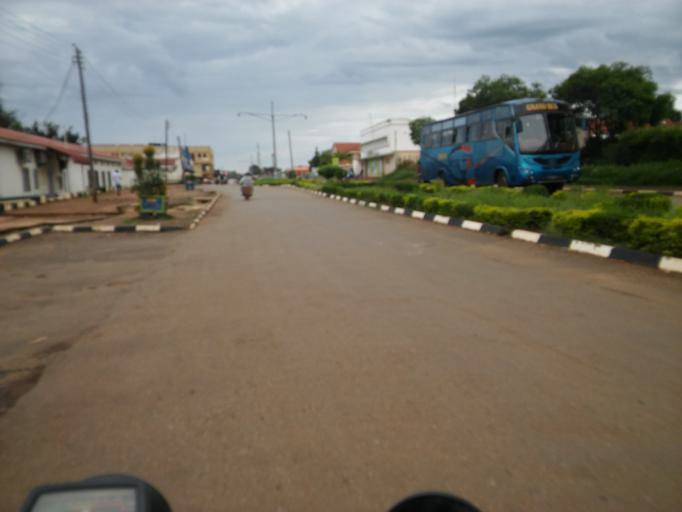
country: UG
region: Eastern Region
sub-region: Mbale District
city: Mbale
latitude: 1.0696
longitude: 34.1808
